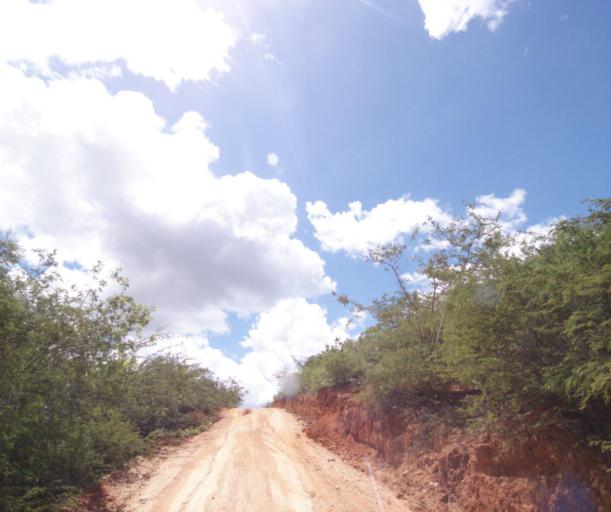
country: BR
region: Bahia
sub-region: Pocoes
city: Pocoes
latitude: -14.3908
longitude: -40.5261
